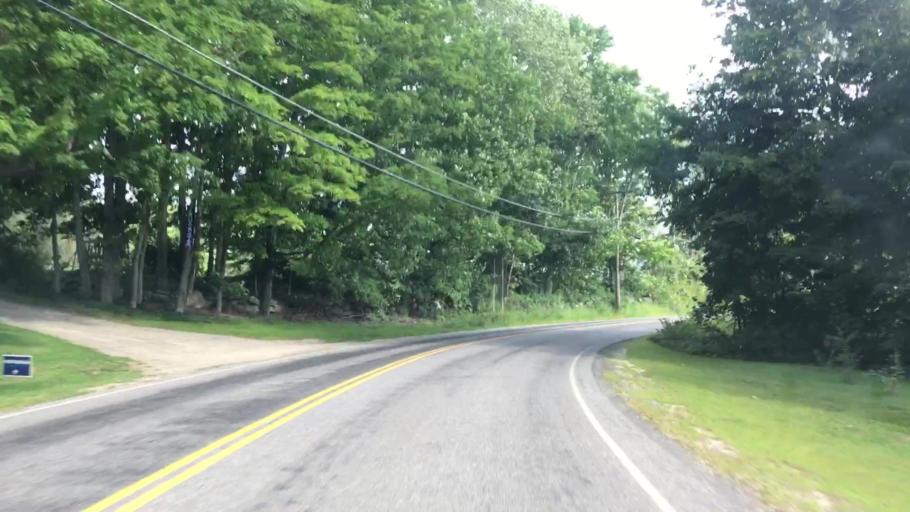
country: US
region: New Hampshire
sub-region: Belknap County
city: Sanbornton
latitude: 43.4887
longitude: -71.5823
